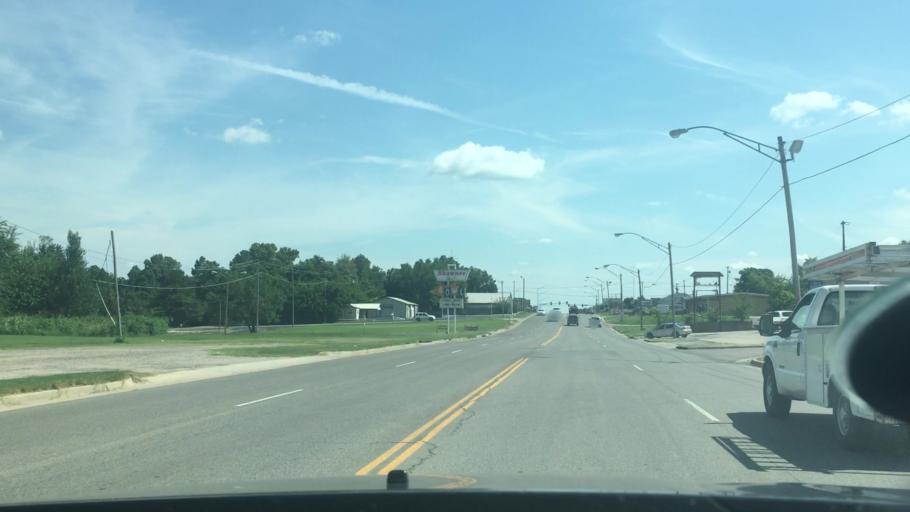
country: US
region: Oklahoma
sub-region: Pottawatomie County
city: Shawnee
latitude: 35.3362
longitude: -96.9122
